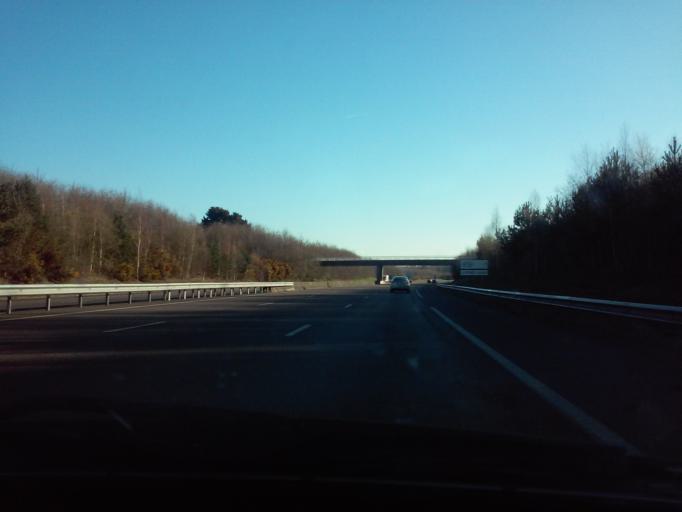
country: FR
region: Brittany
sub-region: Departement d'Ille-et-Vilaine
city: Fouillard
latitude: 48.1625
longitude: -1.5918
